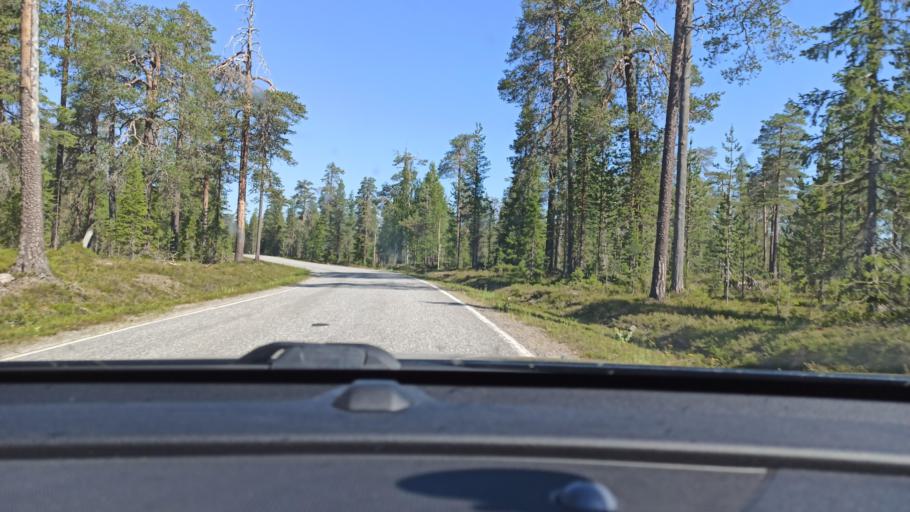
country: FI
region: Lapland
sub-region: Tunturi-Lappi
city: Kolari
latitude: 67.6592
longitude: 24.1657
